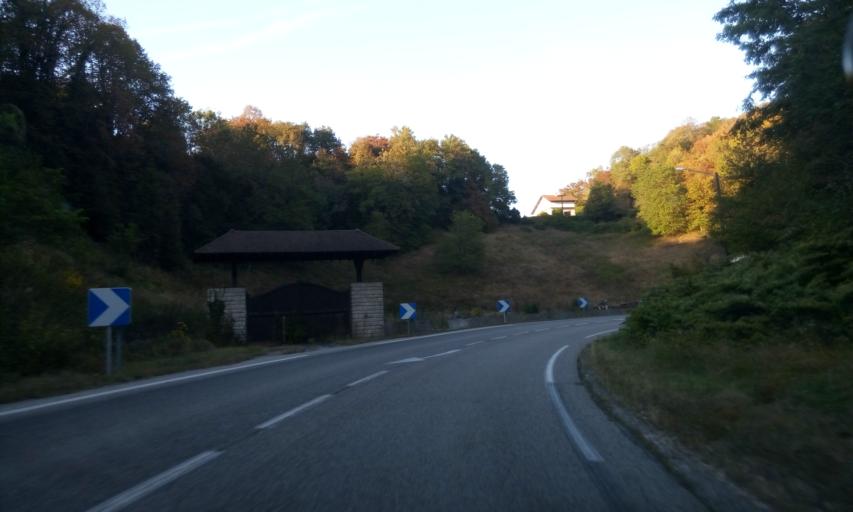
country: FR
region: Rhone-Alpes
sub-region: Departement de l'Ain
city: Saint-Martin-du-Frene
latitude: 46.1167
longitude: 5.4981
